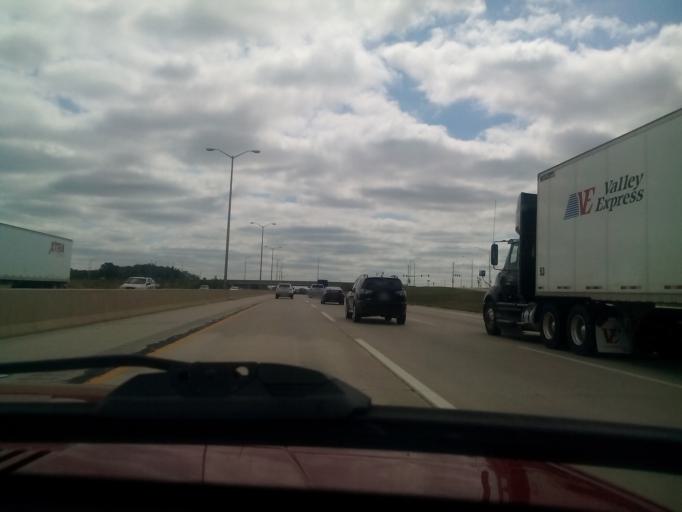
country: US
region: Illinois
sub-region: Cook County
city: Lemont
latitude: 41.6590
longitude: -88.0206
